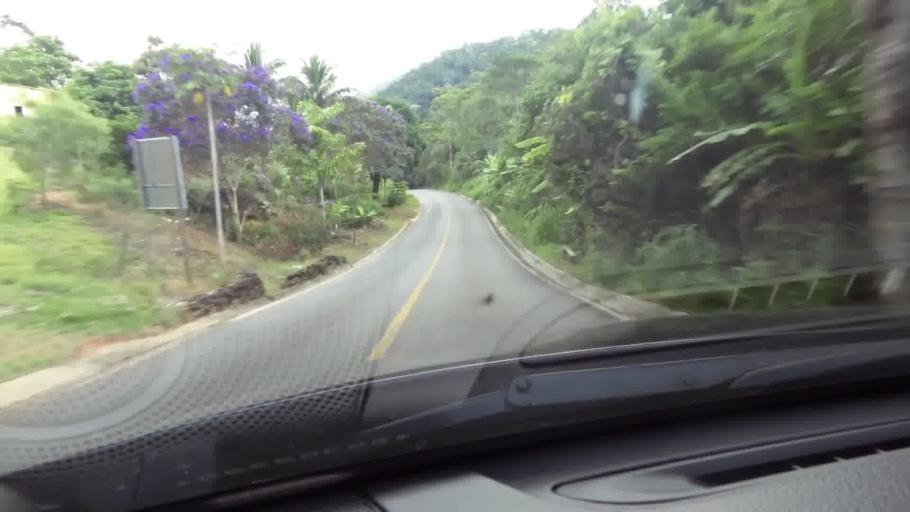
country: BR
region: Espirito Santo
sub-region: Guarapari
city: Guarapari
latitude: -20.5916
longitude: -40.5387
